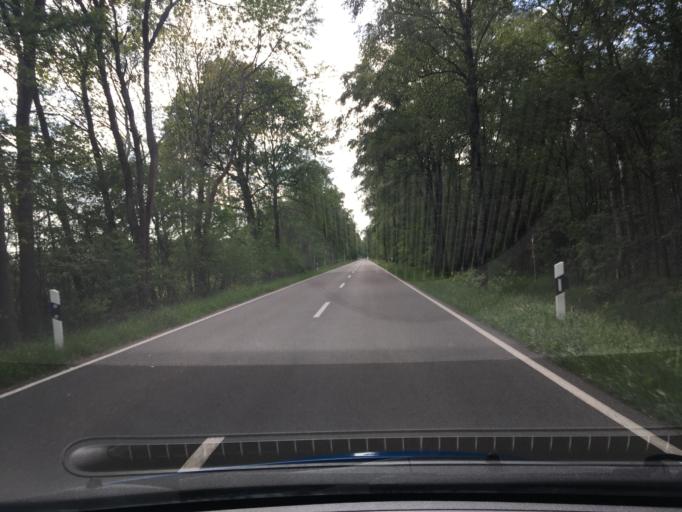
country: DE
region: Lower Saxony
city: Wistedt
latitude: 53.2737
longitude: 9.6399
